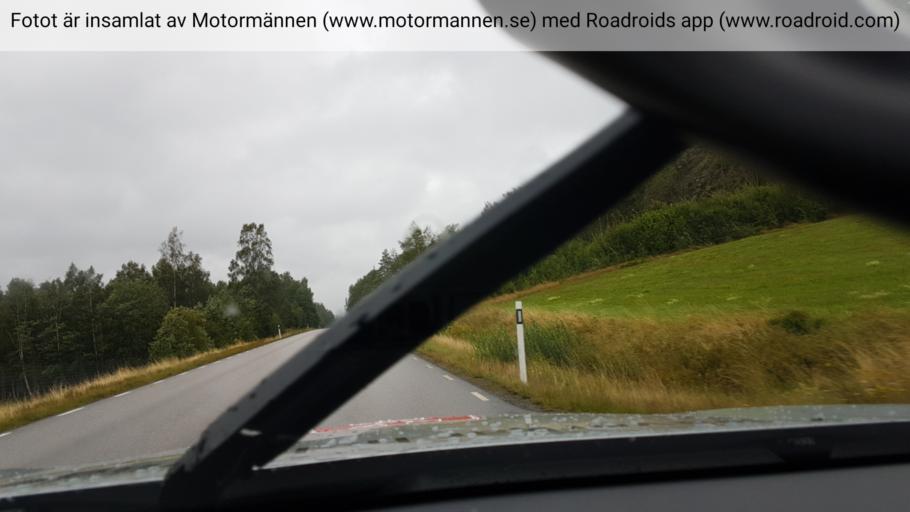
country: SE
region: Vaestra Goetaland
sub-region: Bengtsfors Kommun
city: Billingsfors
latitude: 58.9349
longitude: 12.2126
